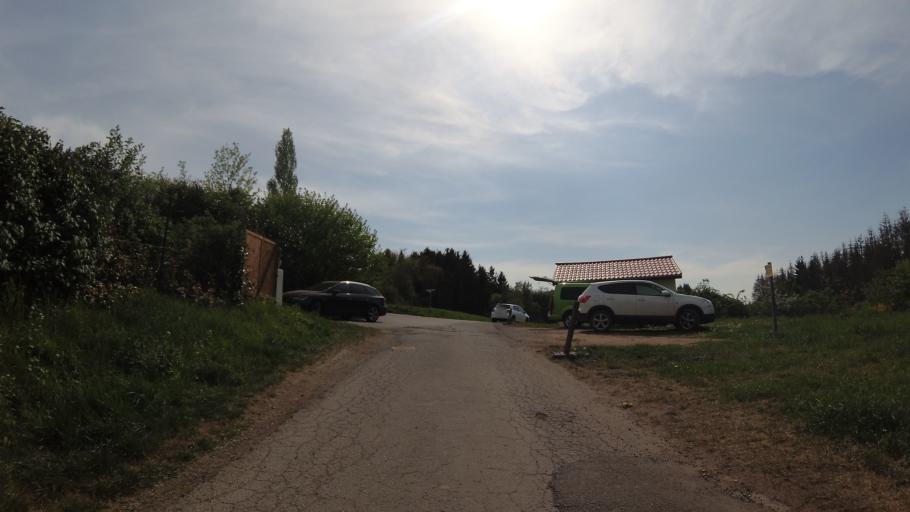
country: DE
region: Saarland
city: Hangard
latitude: 49.3851
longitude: 7.1942
